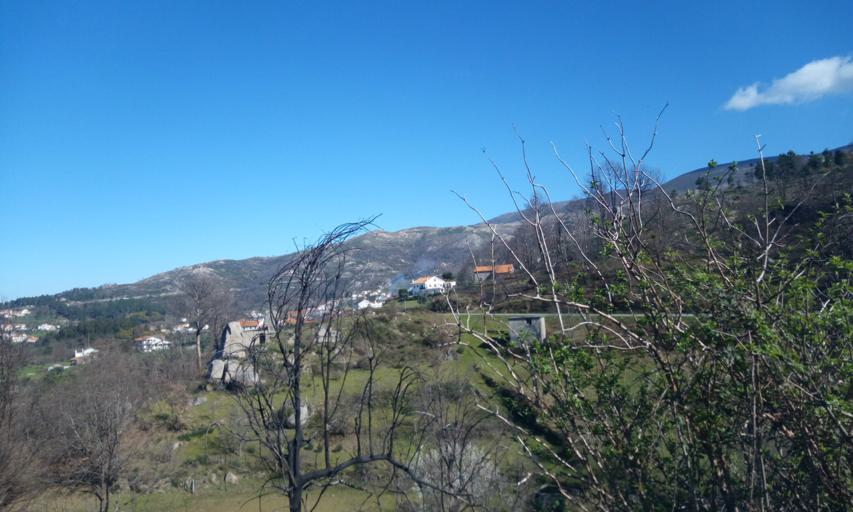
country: PT
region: Guarda
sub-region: Manteigas
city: Manteigas
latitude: 40.4629
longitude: -7.6105
